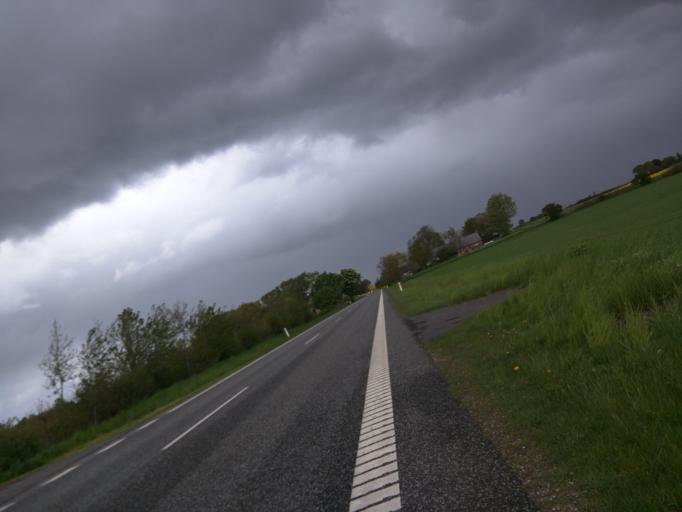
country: DK
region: Central Jutland
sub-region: Silkeborg Kommune
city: Kjellerup
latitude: 56.3419
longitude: 9.4298
